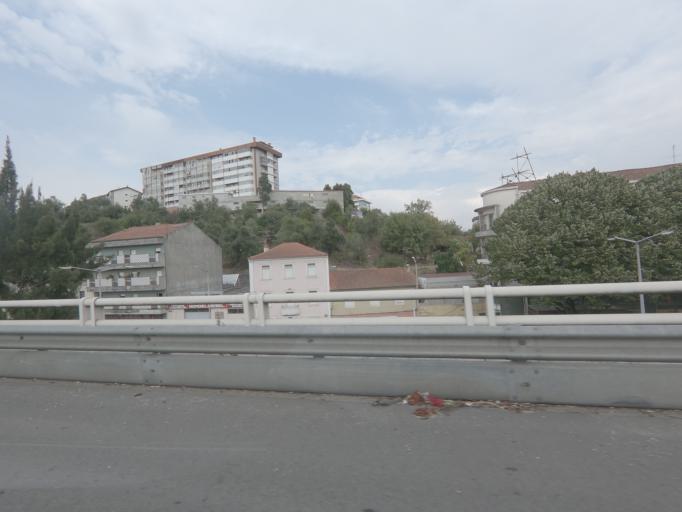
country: PT
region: Coimbra
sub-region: Coimbra
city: Coimbra
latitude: 40.2210
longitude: -8.4393
